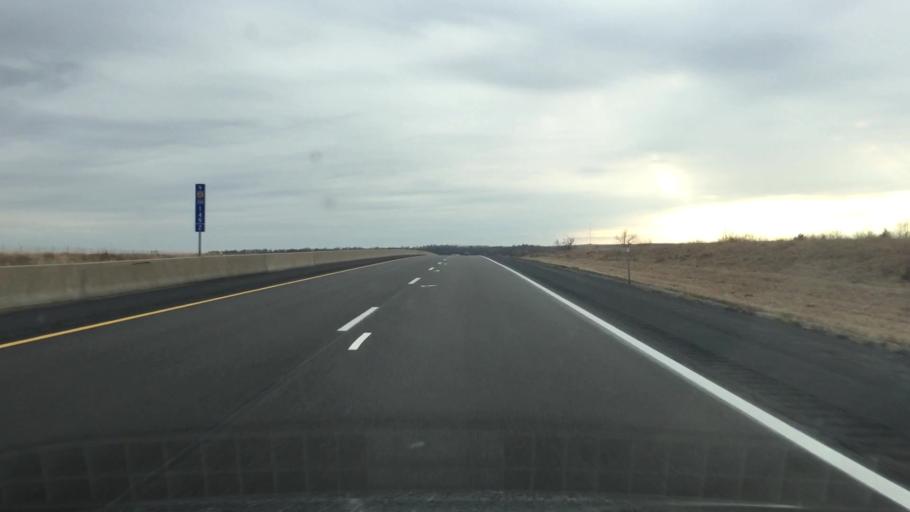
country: US
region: Kansas
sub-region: Osage County
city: Osage City
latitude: 38.6778
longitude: -96.0055
